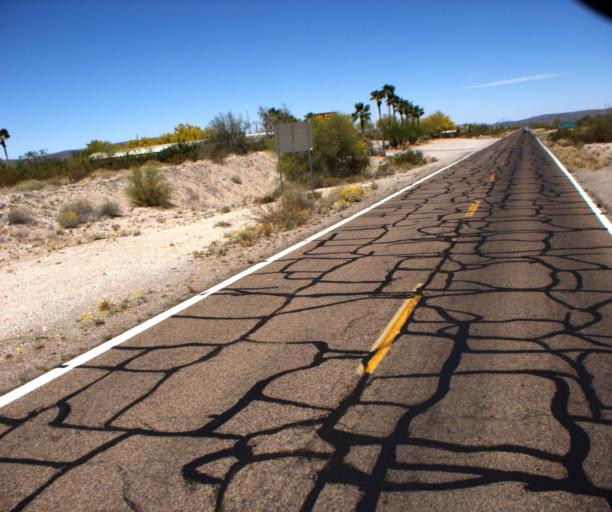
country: US
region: Arizona
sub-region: Pima County
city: Ajo
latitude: 32.4022
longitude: -112.8719
